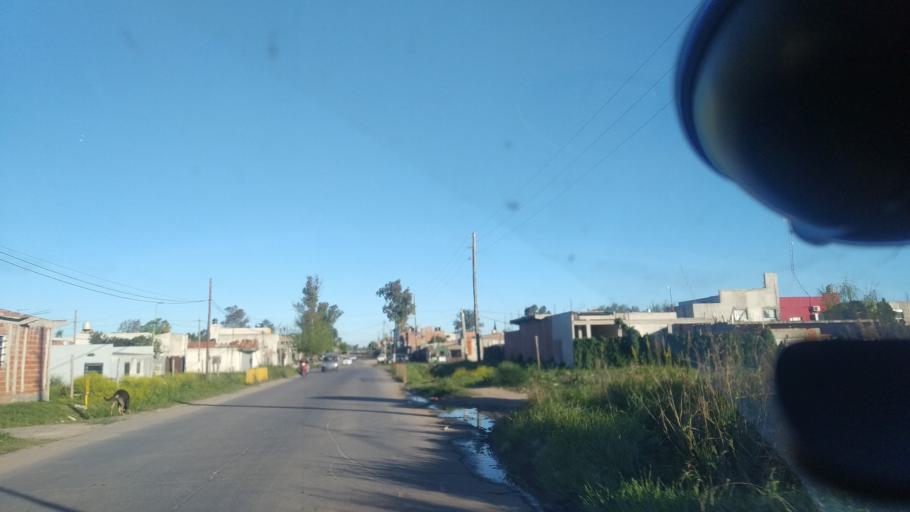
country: AR
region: Buenos Aires
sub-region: Partido de La Plata
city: La Plata
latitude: -34.9646
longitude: -57.9662
